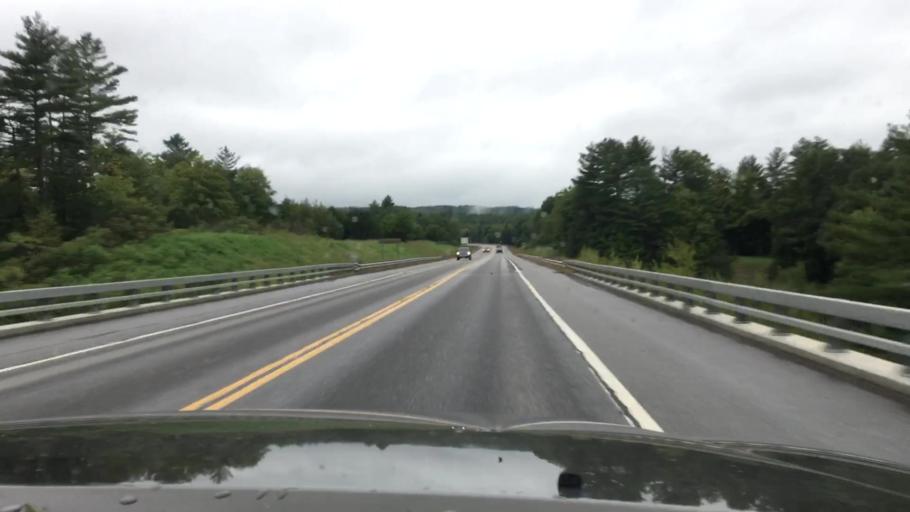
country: US
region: New Hampshire
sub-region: Hillsborough County
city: Hillsborough
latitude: 43.1173
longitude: -71.9296
